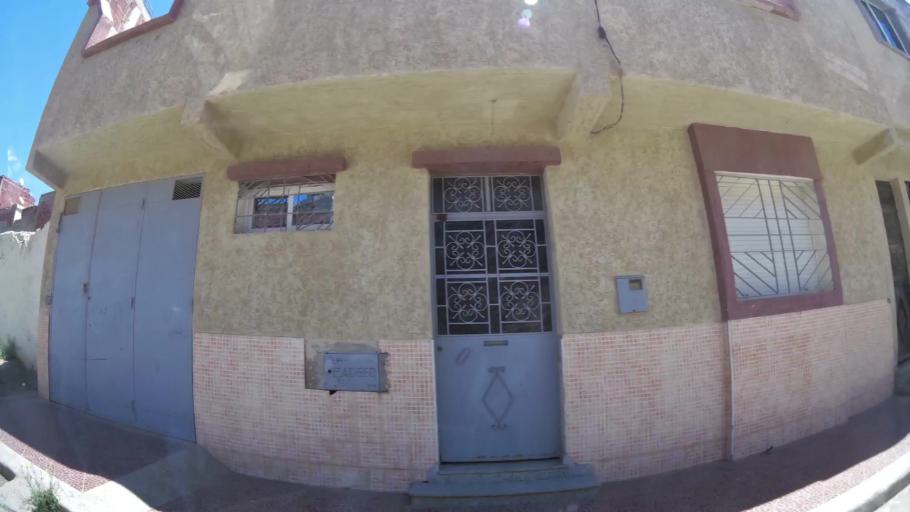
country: MA
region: Oriental
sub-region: Oujda-Angad
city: Oujda
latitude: 34.6629
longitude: -1.9249
